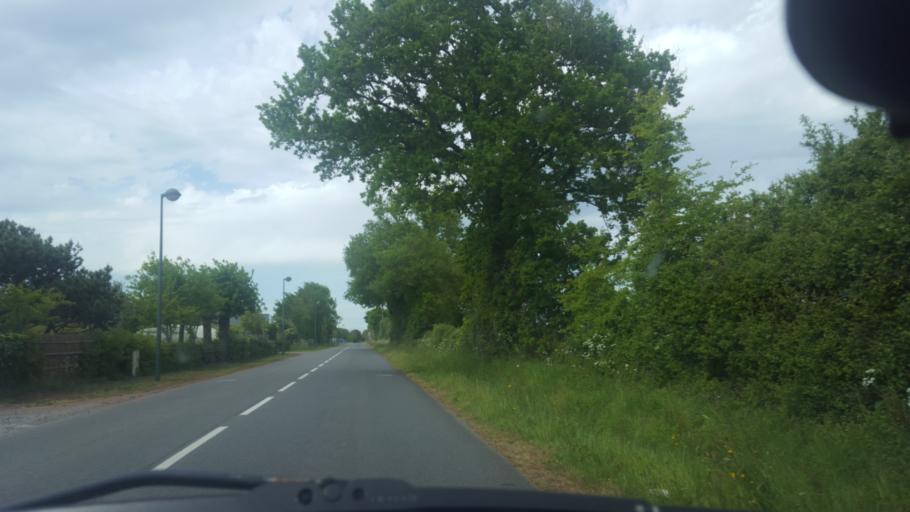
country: FR
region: Pays de la Loire
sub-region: Departement de la Loire-Atlantique
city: Paulx
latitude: 46.9664
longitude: -1.7550
